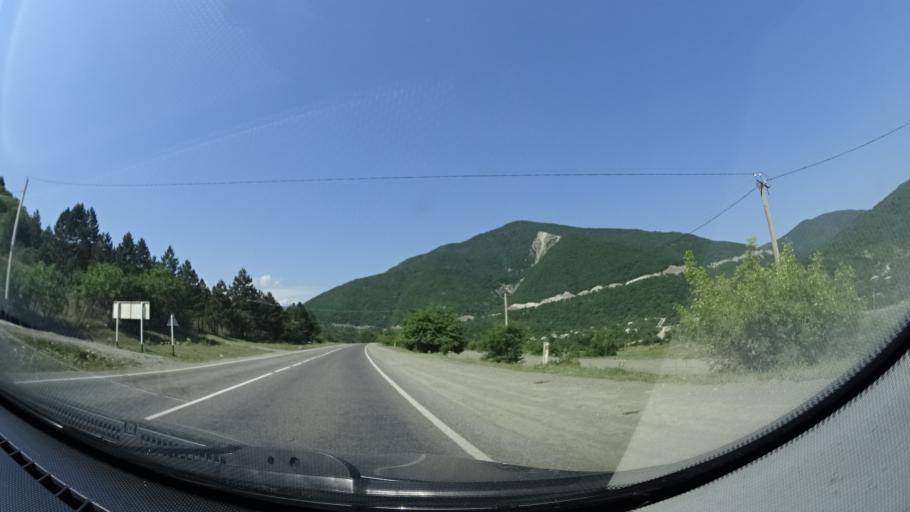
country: GE
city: Zhinvali
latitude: 42.1192
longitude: 44.7756
